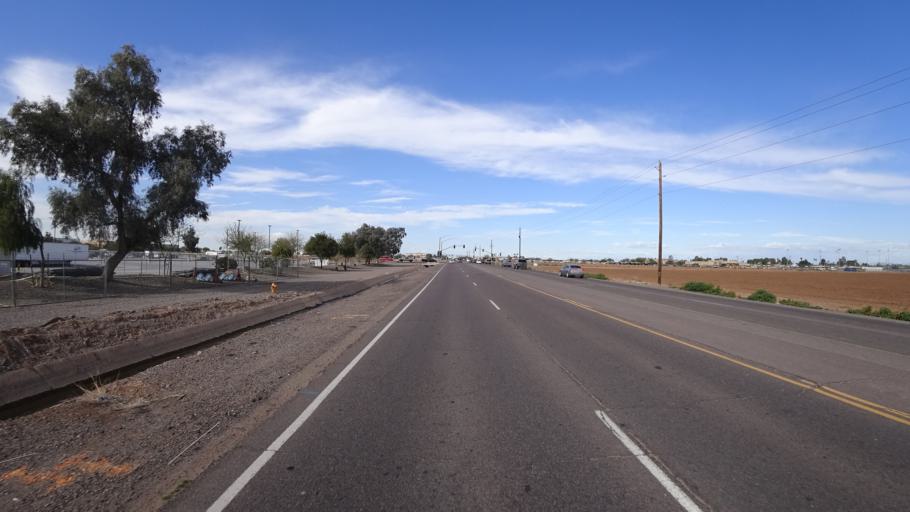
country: US
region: Arizona
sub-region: Maricopa County
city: Tolleson
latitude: 33.4456
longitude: -112.2725
